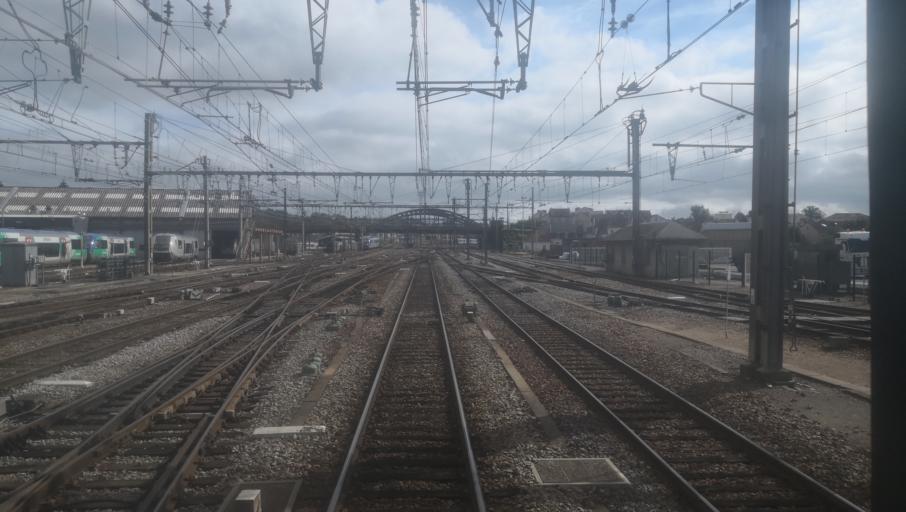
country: FR
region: Limousin
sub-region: Departement de la Haute-Vienne
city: Limoges
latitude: 45.8392
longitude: 1.2708
